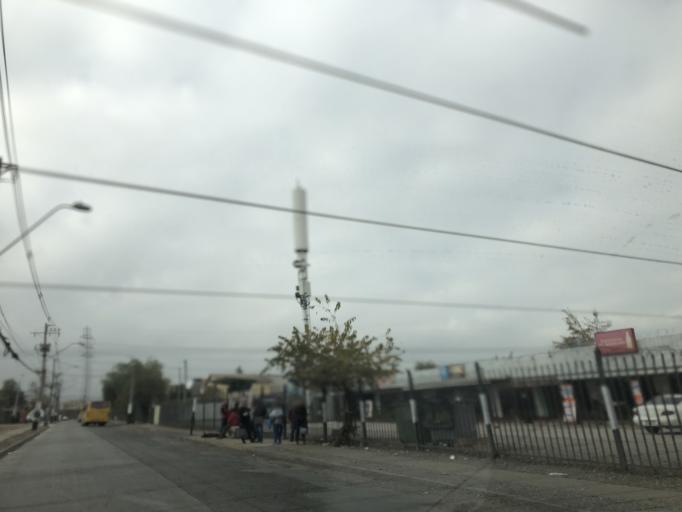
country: CL
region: Santiago Metropolitan
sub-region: Provincia de Cordillera
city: Puente Alto
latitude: -33.5937
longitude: -70.6022
